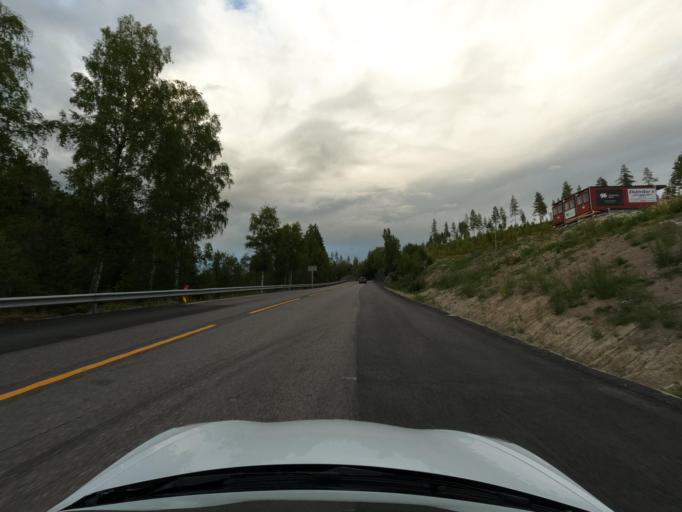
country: NO
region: Telemark
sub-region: Notodden
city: Notodden
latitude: 59.5746
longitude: 9.2928
